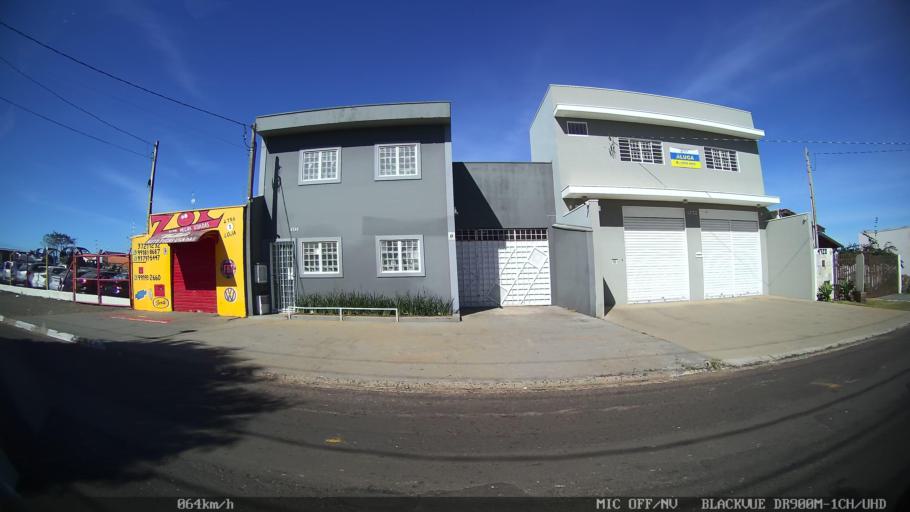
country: BR
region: Sao Paulo
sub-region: Franca
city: Franca
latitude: -20.5404
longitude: -47.3657
